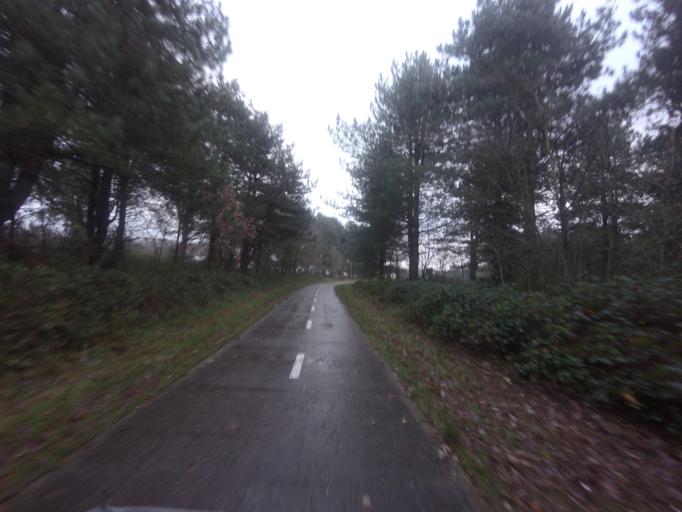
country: NL
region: North Holland
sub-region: Gemeente Texel
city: Den Burg
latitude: 53.1554
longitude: 4.8623
